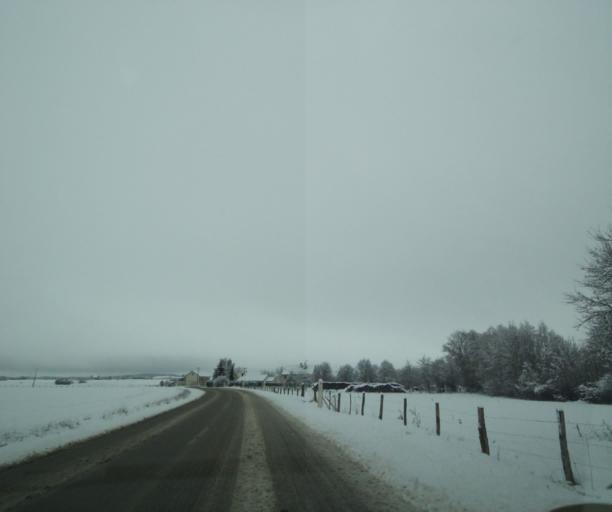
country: FR
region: Champagne-Ardenne
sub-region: Departement de la Haute-Marne
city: Wassy
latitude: 48.5319
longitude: 4.9253
